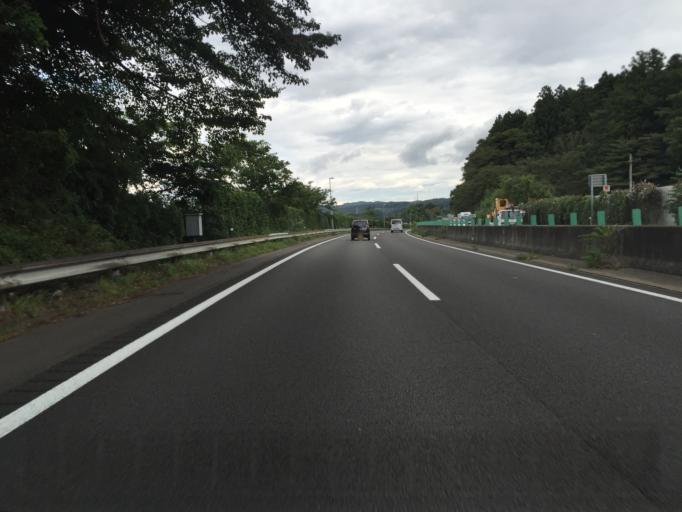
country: JP
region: Miyagi
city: Okawara
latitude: 38.1031
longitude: 140.6890
